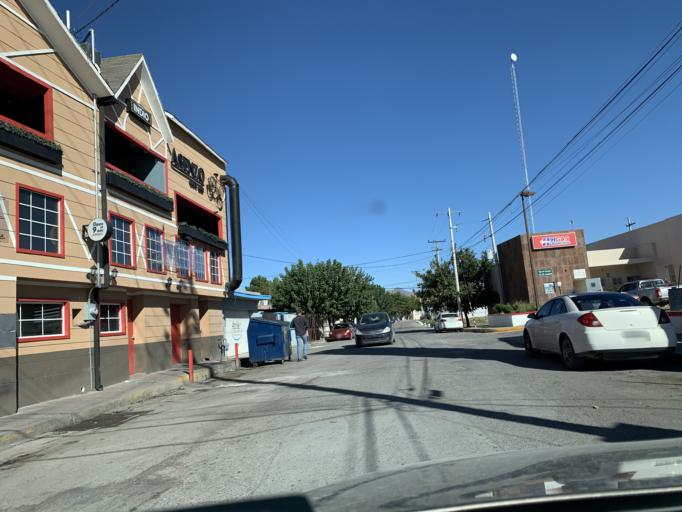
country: MX
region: Chihuahua
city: Ciudad Juarez
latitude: 31.7373
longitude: -106.4440
